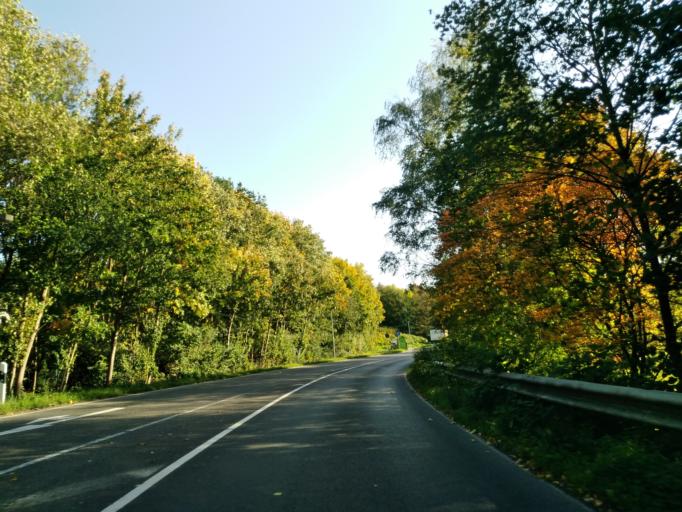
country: DE
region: Rheinland-Pfalz
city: Asbach
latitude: 50.7384
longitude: 7.3662
